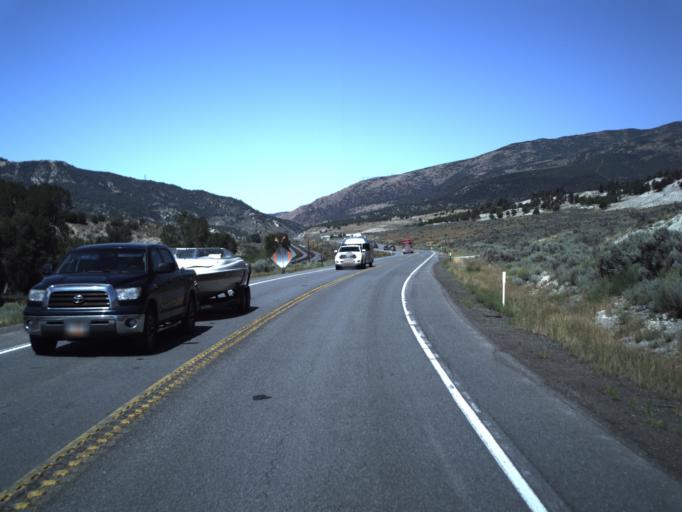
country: US
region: Utah
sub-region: Utah County
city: Mapleton
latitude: 39.9664
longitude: -111.3215
